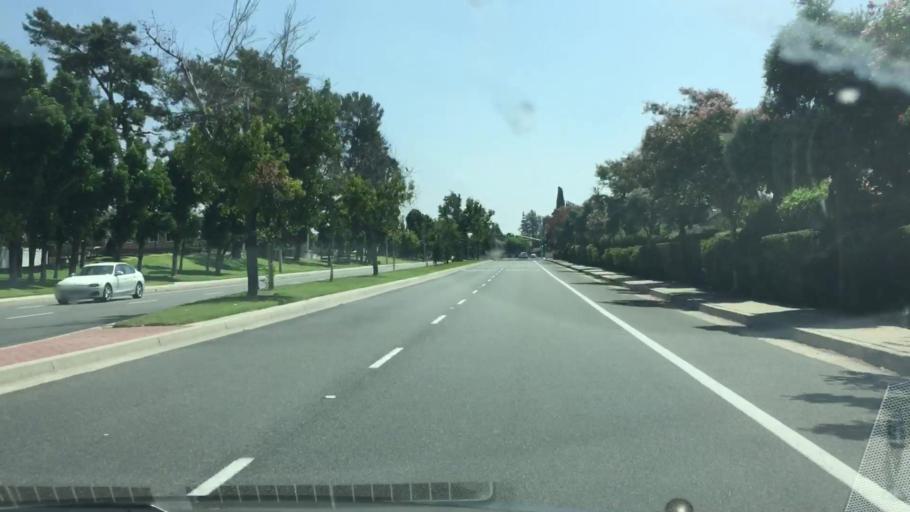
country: US
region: California
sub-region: Orange County
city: Irvine
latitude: 33.6960
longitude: -117.7752
